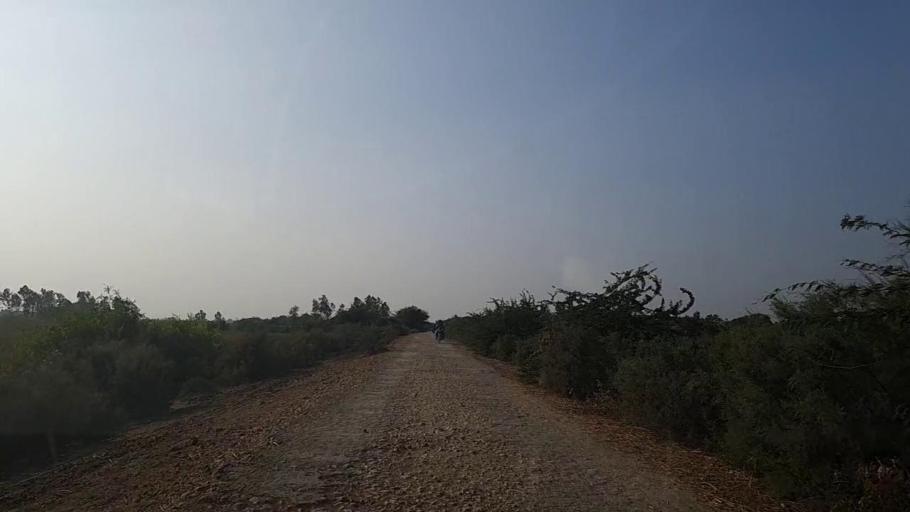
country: PK
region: Sindh
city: Mirpur Sakro
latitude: 24.5700
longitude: 67.6682
